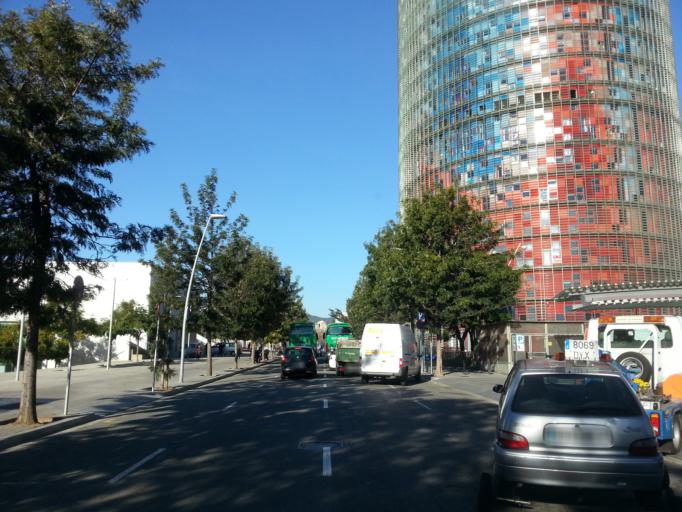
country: ES
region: Catalonia
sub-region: Provincia de Barcelona
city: Sant Marti
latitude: 41.4028
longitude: 2.1900
